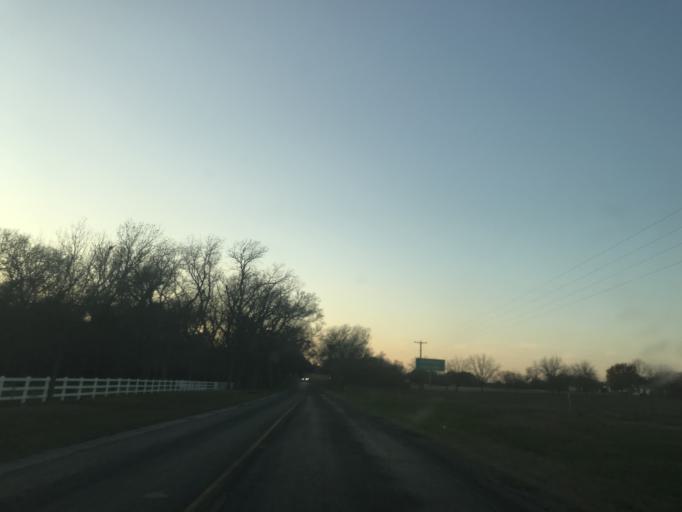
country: US
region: Texas
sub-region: Williamson County
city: Hutto
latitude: 30.4938
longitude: -97.4939
